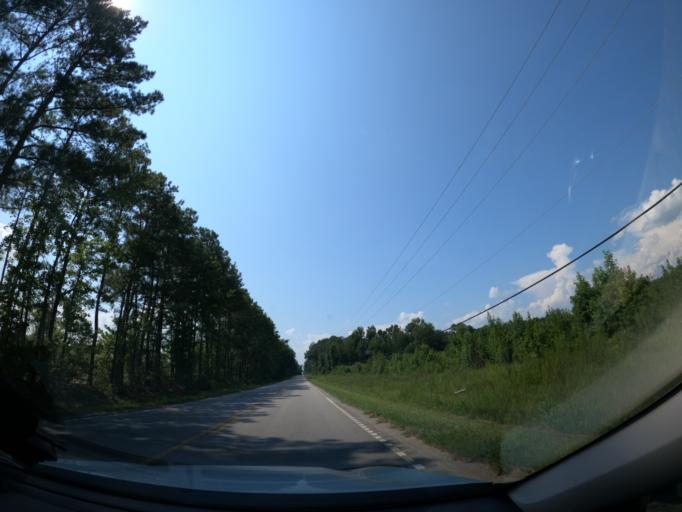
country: US
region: South Carolina
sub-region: Richland County
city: Hopkins
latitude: 33.9065
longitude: -80.9320
